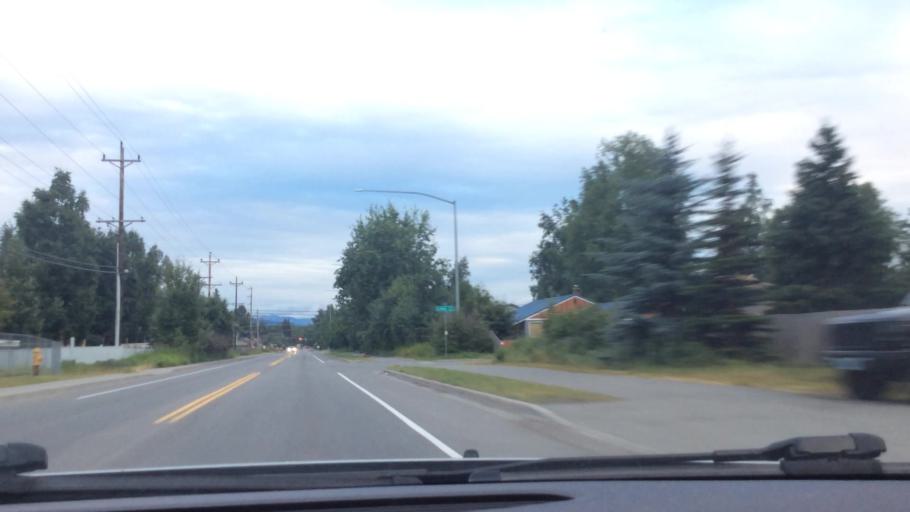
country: US
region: Alaska
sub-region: Anchorage Municipality
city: Elmendorf Air Force Base
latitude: 61.2153
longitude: -149.7560
